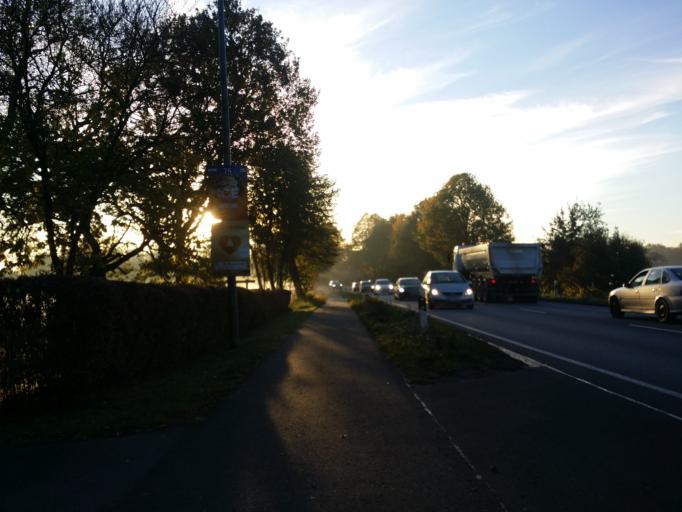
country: DE
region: Lower Saxony
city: Kirchseelte
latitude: 52.9965
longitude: 8.7101
